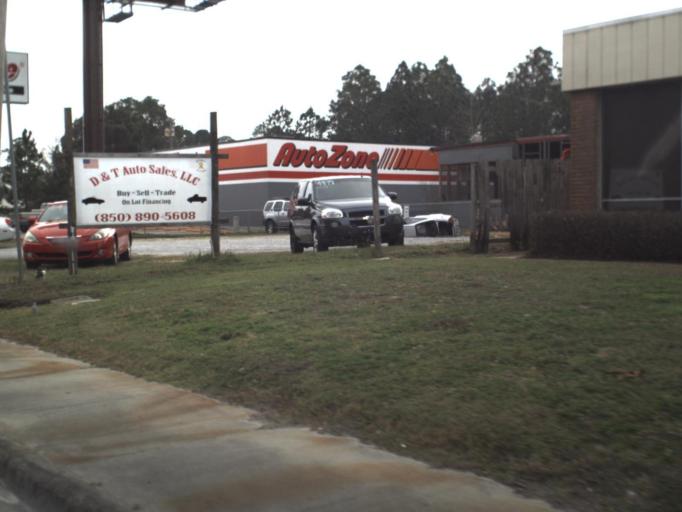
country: US
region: Florida
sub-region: Bay County
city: Parker
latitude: 30.1345
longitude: -85.5913
